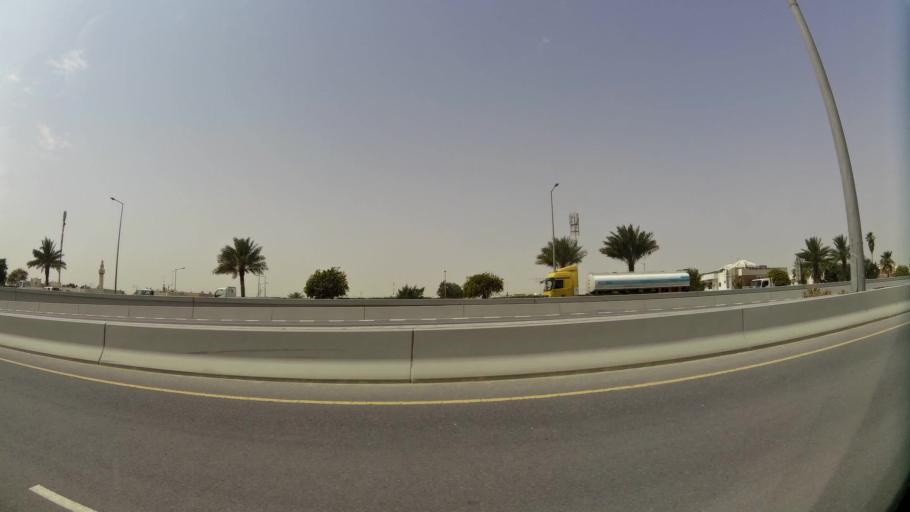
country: QA
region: Baladiyat ar Rayyan
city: Ar Rayyan
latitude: 25.2284
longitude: 51.4314
